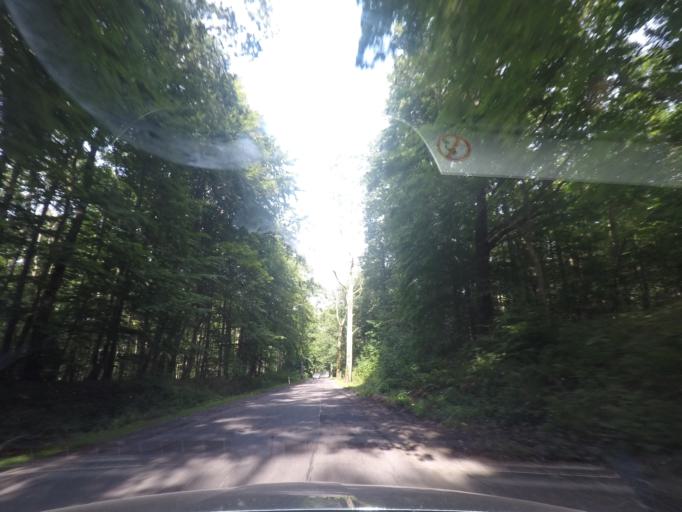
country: PL
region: Pomeranian Voivodeship
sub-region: Powiat slupski
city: Glowczyce
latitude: 54.6066
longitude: 17.3254
